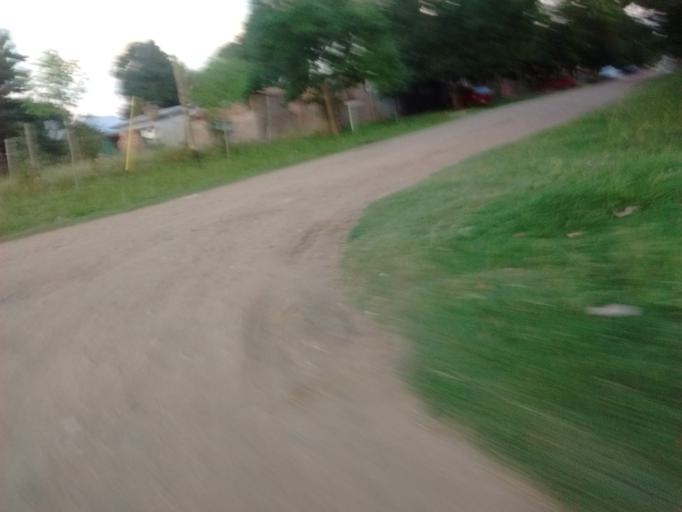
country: AR
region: Santa Fe
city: Funes
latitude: -32.9092
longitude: -60.8160
